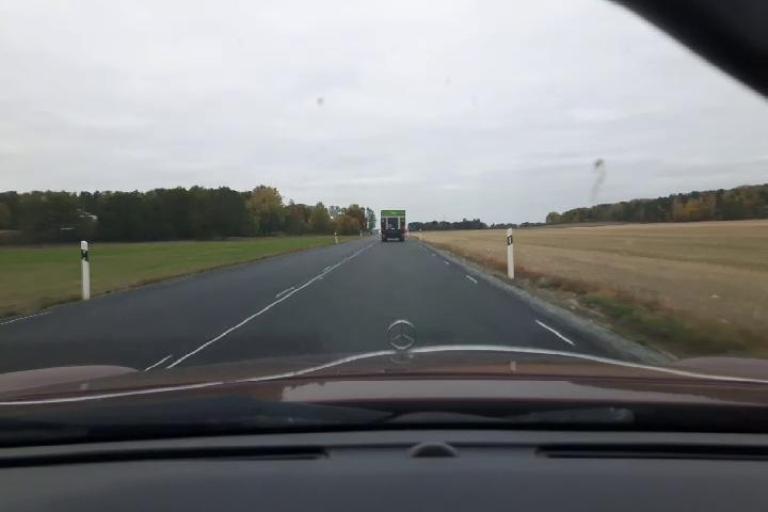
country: SE
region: Uppsala
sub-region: Enkopings Kommun
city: Enkoping
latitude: 59.6030
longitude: 17.0208
